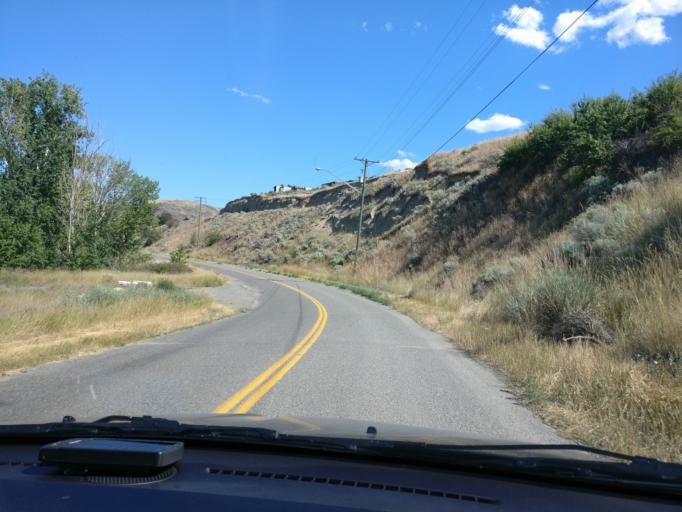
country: CA
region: British Columbia
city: Logan Lake
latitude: 50.7528
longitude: -120.8591
